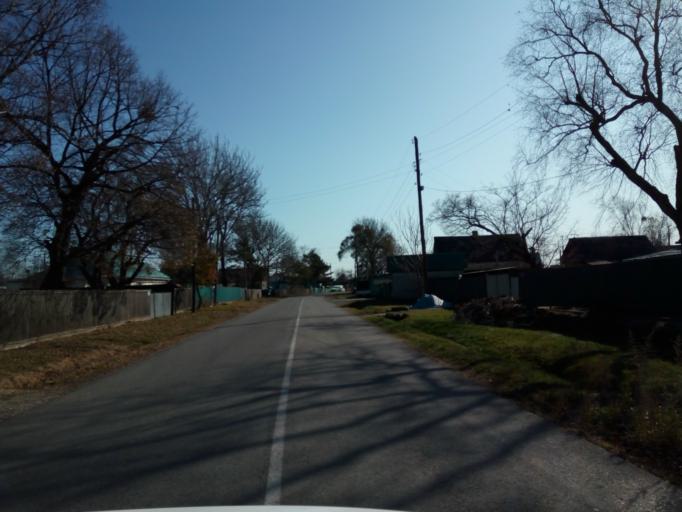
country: RU
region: Primorskiy
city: Dal'nerechensk
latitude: 45.9389
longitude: 133.6983
